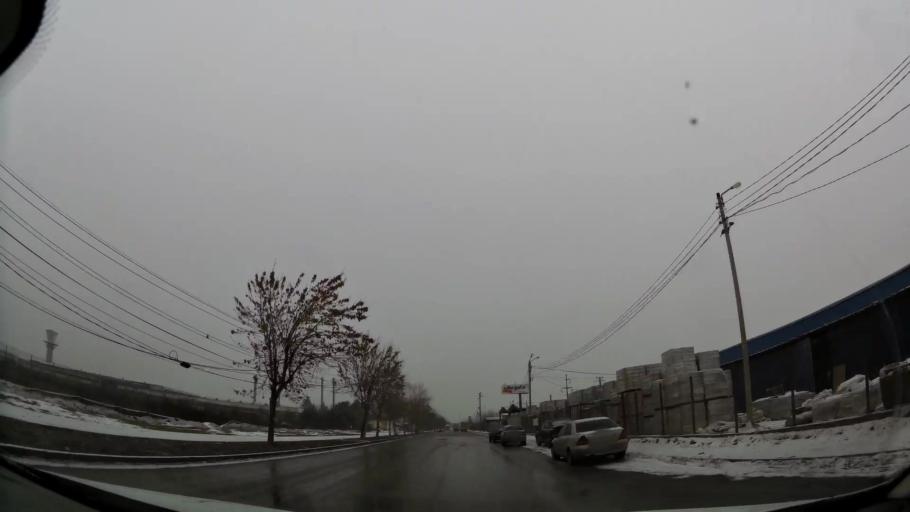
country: RO
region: Dambovita
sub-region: Municipiul Targoviste
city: Targoviste
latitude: 44.9184
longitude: 25.4376
